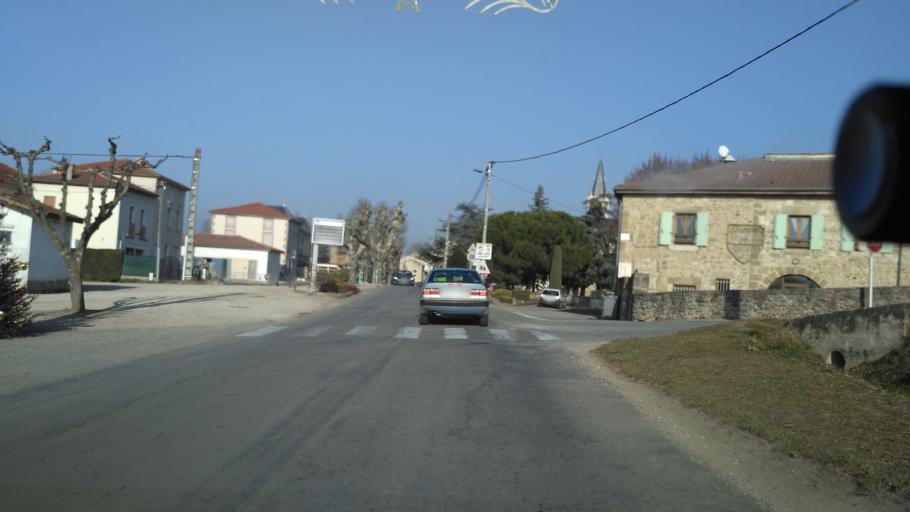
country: FR
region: Rhone-Alpes
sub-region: Departement de la Drome
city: Clerieux
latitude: 45.0741
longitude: 4.9587
